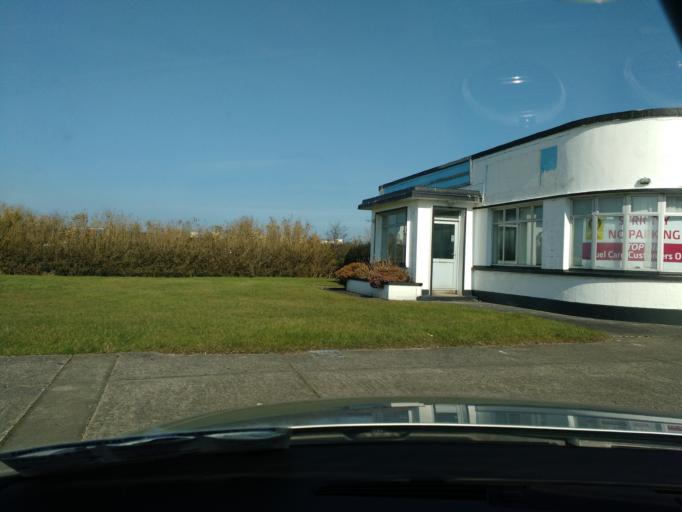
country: IE
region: Munster
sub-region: An Clar
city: Shannon
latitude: 52.6943
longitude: -8.9020
